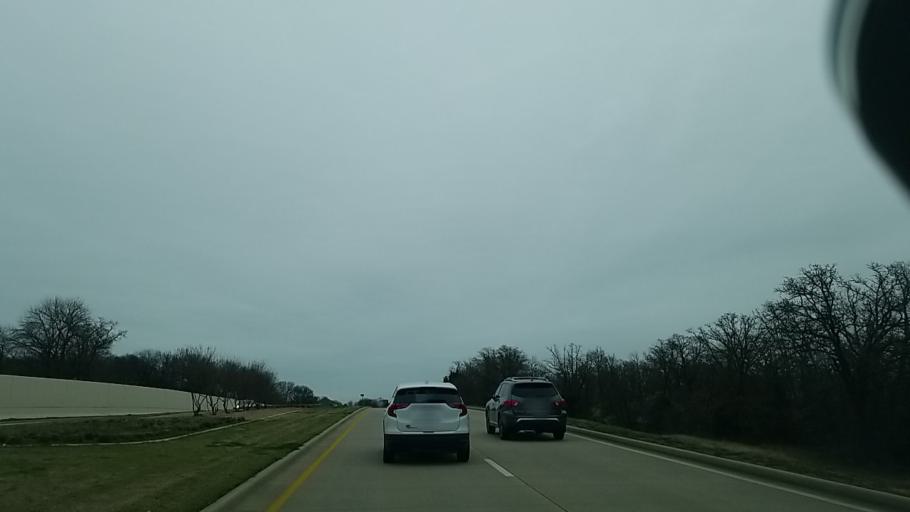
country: US
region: Texas
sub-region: Denton County
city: Copper Canyon
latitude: 33.1263
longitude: -97.0898
